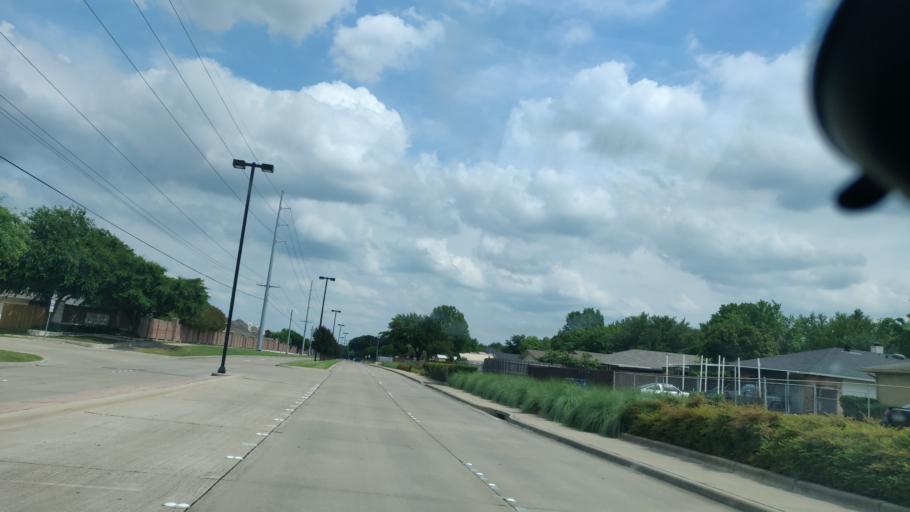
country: US
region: Texas
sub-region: Dallas County
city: Garland
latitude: 32.9404
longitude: -96.6123
